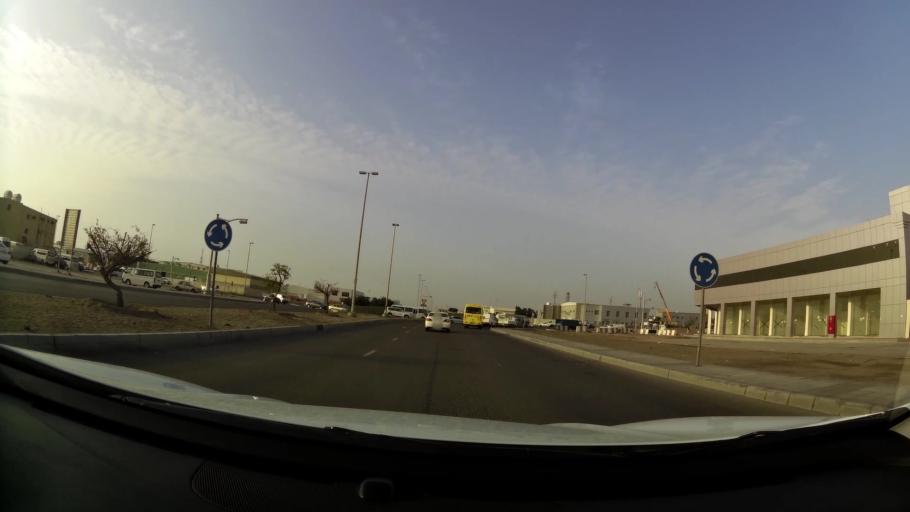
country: AE
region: Abu Dhabi
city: Abu Dhabi
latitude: 24.3674
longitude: 54.5015
